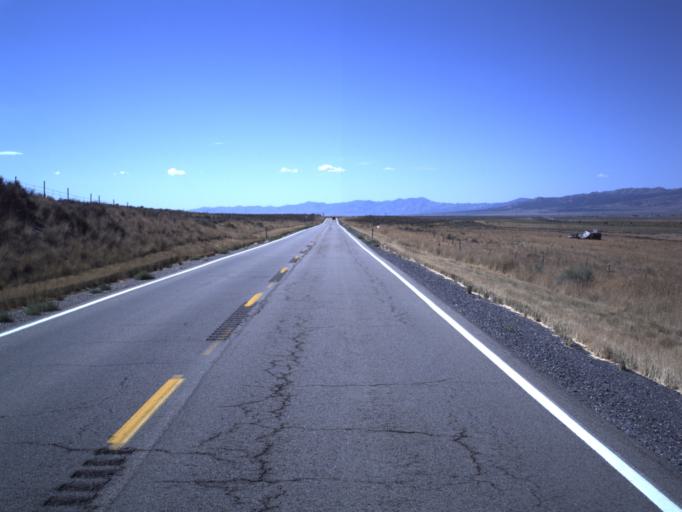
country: US
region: Utah
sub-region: Tooele County
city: Tooele
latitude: 40.4187
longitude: -112.3824
